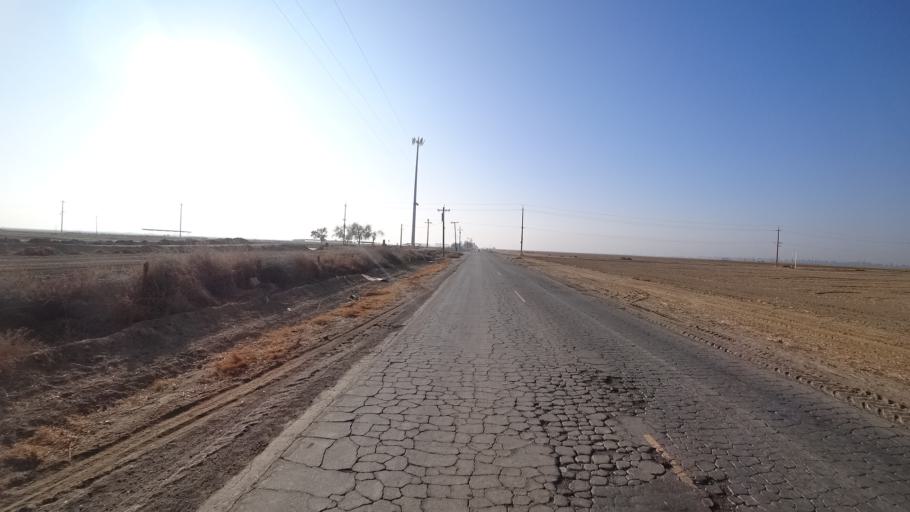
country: US
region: California
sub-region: Kern County
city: Weedpatch
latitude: 35.2242
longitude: -118.9676
